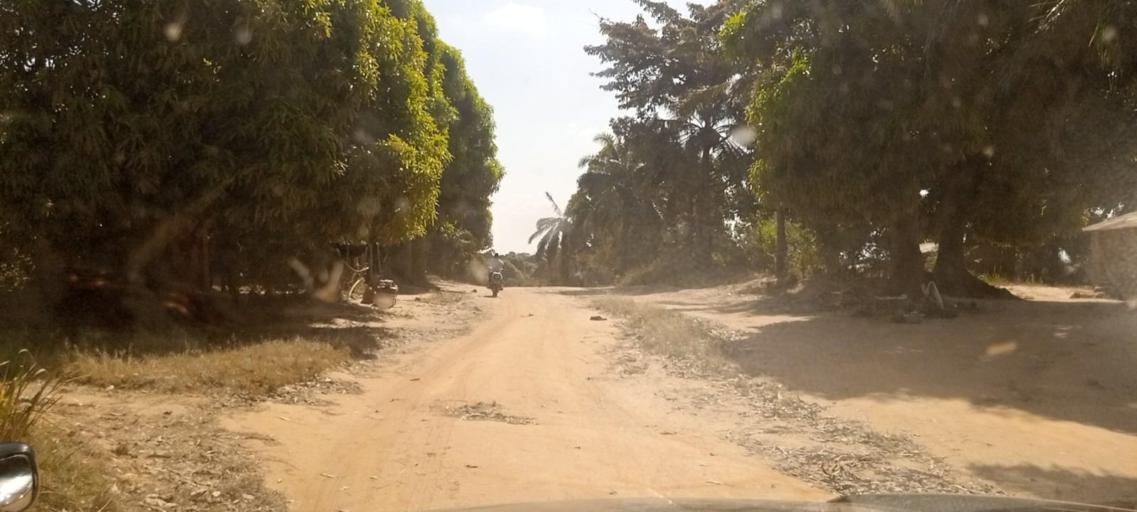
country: CD
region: Kasai-Oriental
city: Kabinda
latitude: -6.1325
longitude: 24.5097
